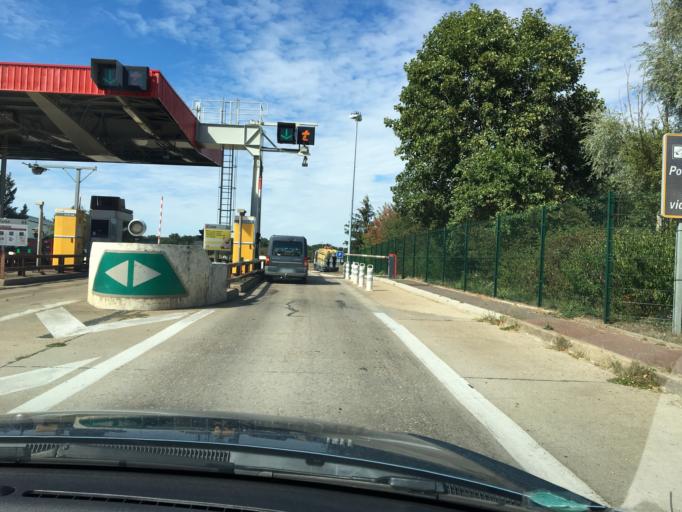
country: FR
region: Bourgogne
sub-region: Departement de l'Yonne
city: Gurgy
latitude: 47.8513
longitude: 3.5489
